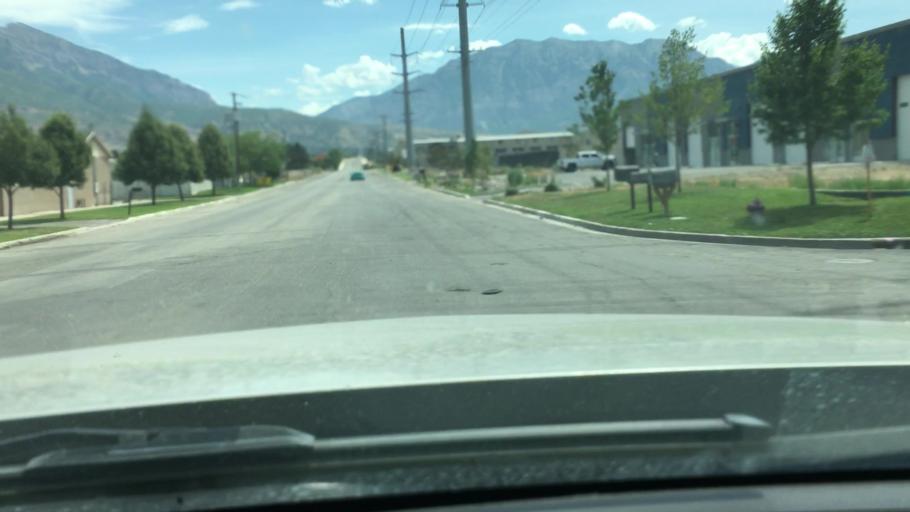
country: US
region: Utah
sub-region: Utah County
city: Pleasant Grove
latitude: 40.3335
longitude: -111.7536
